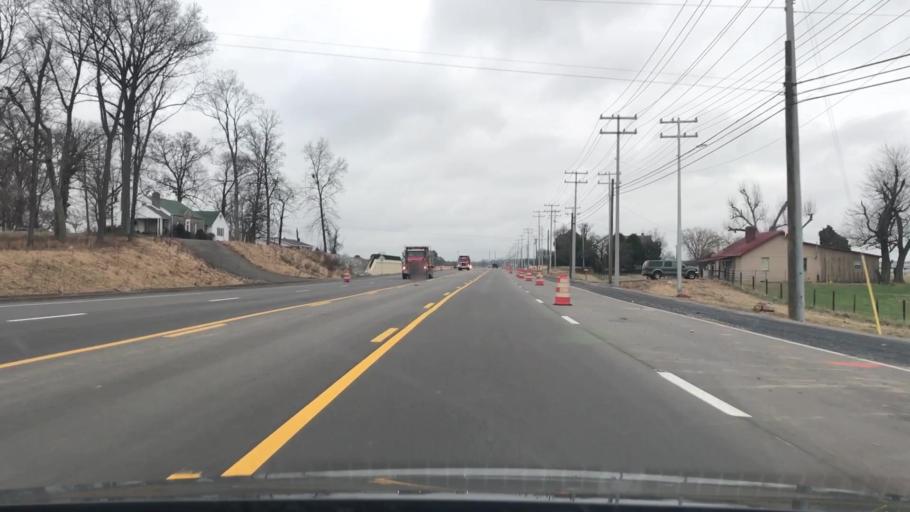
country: US
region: Kentucky
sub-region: Todd County
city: Guthrie
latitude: 36.6074
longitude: -87.2732
